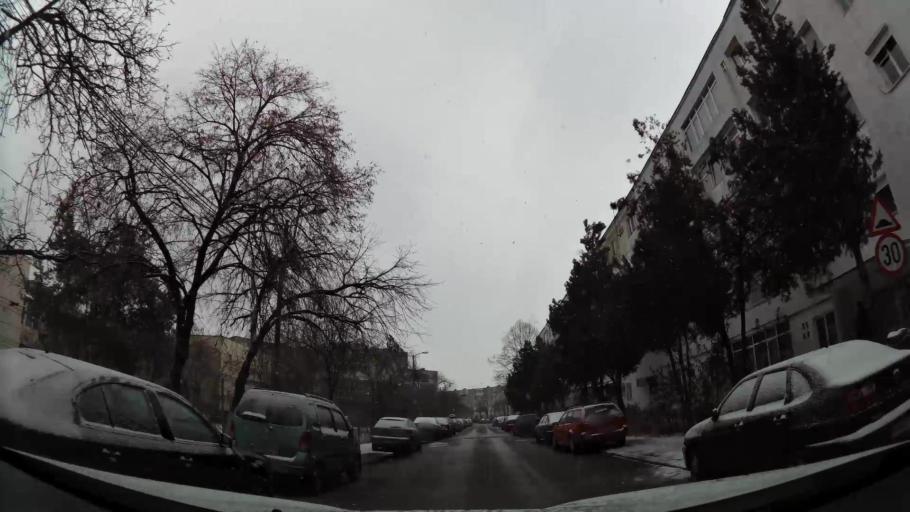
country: RO
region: Prahova
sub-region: Comuna Targsoru Vechi
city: Strejnicu
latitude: 44.9346
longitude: 25.9826
